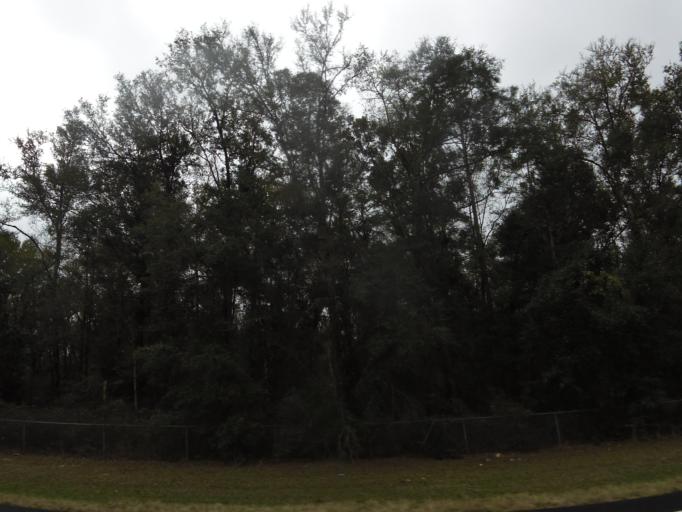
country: US
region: Florida
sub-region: Alachua County
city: High Springs
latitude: 29.8156
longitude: -82.6973
